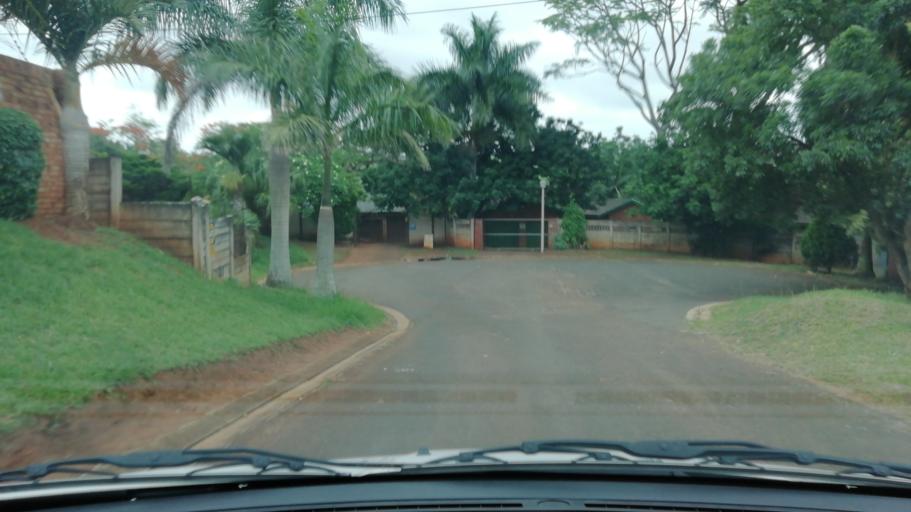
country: ZA
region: KwaZulu-Natal
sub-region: uThungulu District Municipality
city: Empangeni
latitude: -28.7649
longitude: 31.8875
